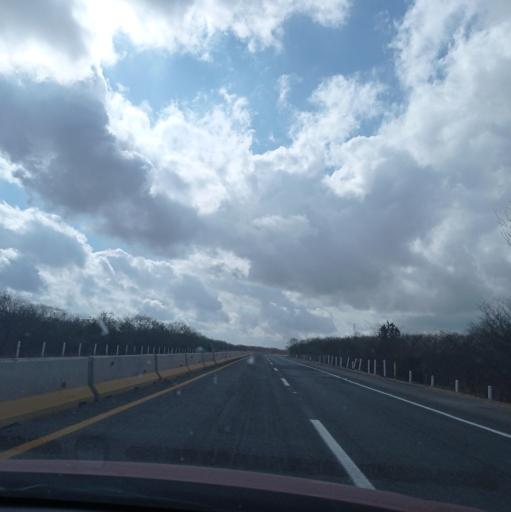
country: MX
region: Sinaloa
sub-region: Navolato
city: Juan Aldama (El Tigre)
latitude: 24.9949
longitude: -107.7767
